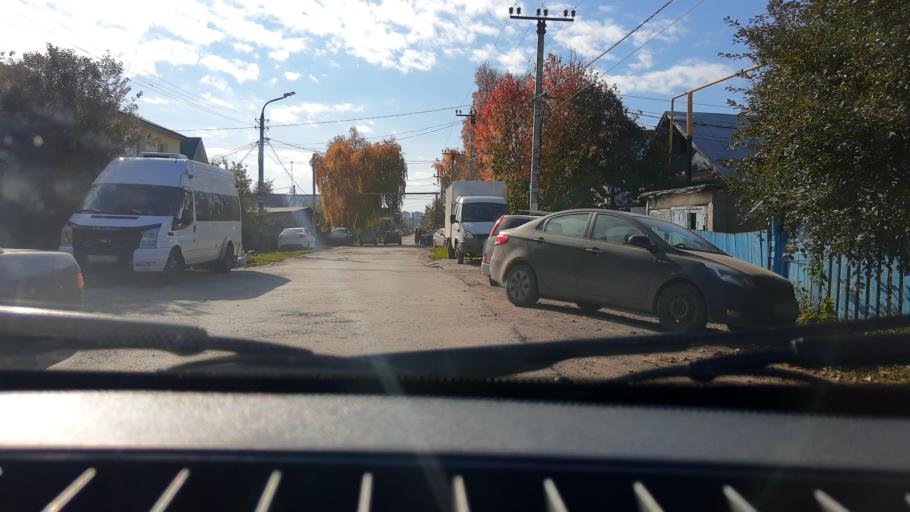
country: RU
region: Bashkortostan
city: Ufa
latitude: 54.7809
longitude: 56.0648
